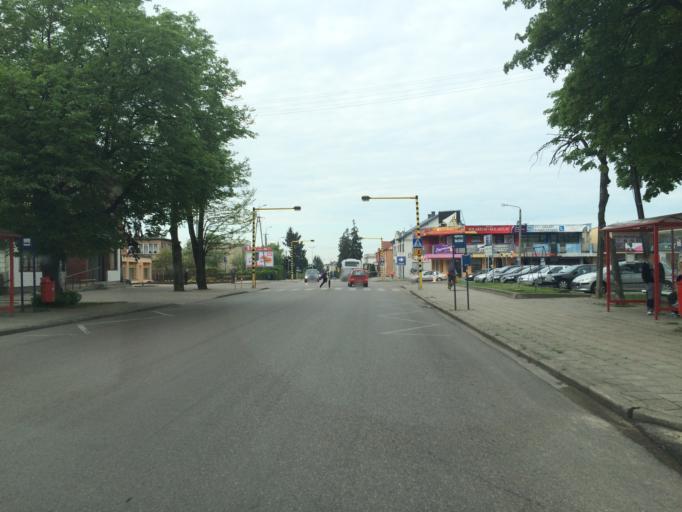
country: PL
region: Masovian Voivodeship
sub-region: Powiat mlawski
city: Mlawa
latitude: 53.1108
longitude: 20.3742
